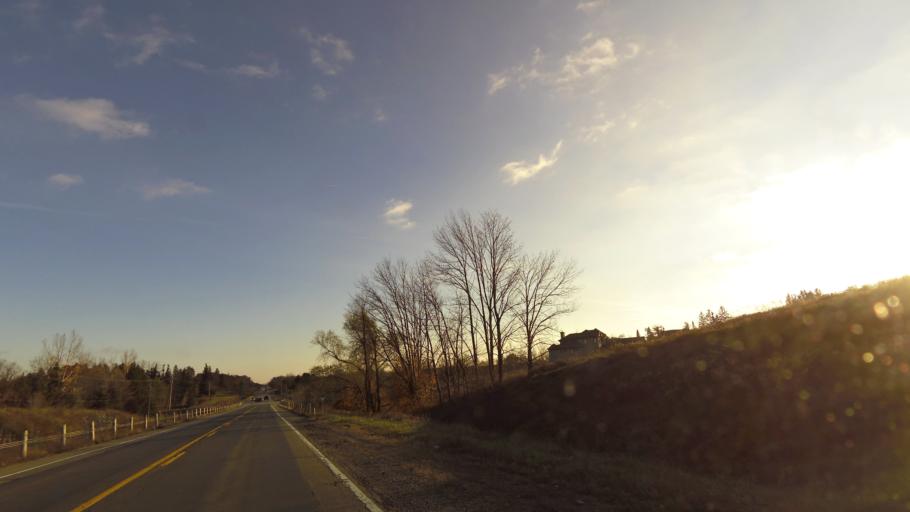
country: CA
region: Ontario
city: Cambridge
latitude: 43.2679
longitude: -80.3015
